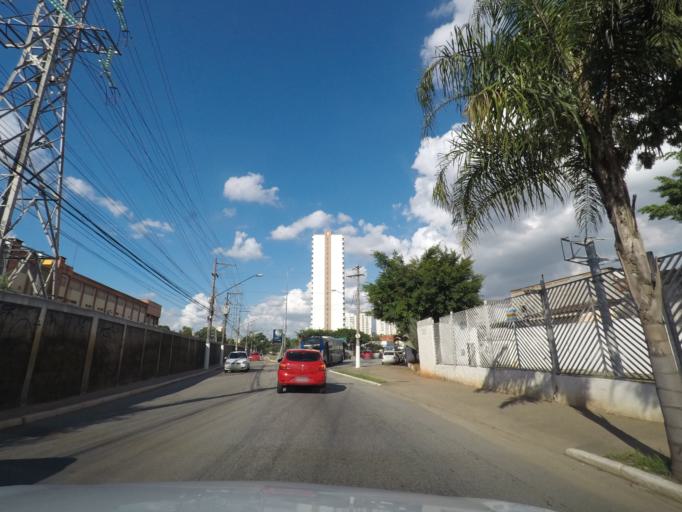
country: BR
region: Sao Paulo
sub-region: Sao Paulo
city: Sao Paulo
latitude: -23.5041
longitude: -46.6826
